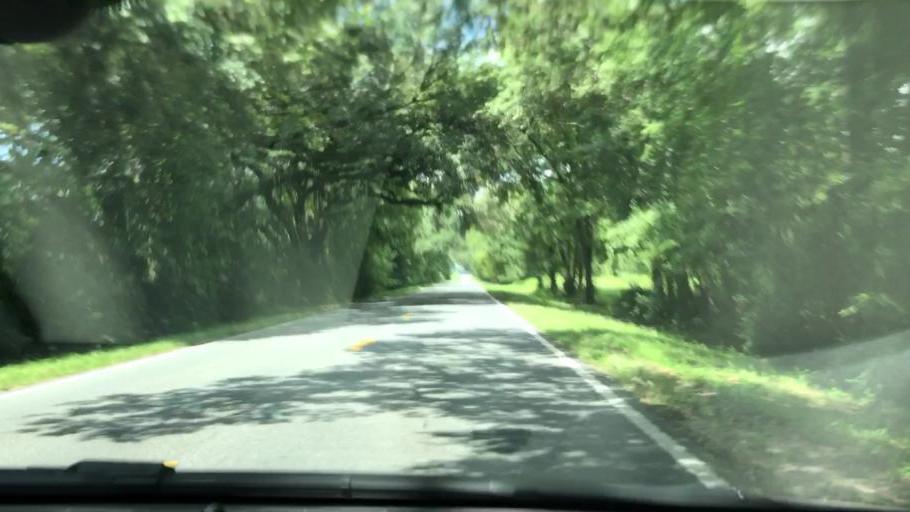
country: US
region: Florida
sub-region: Jackson County
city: Malone
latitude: 30.9454
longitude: -85.1183
